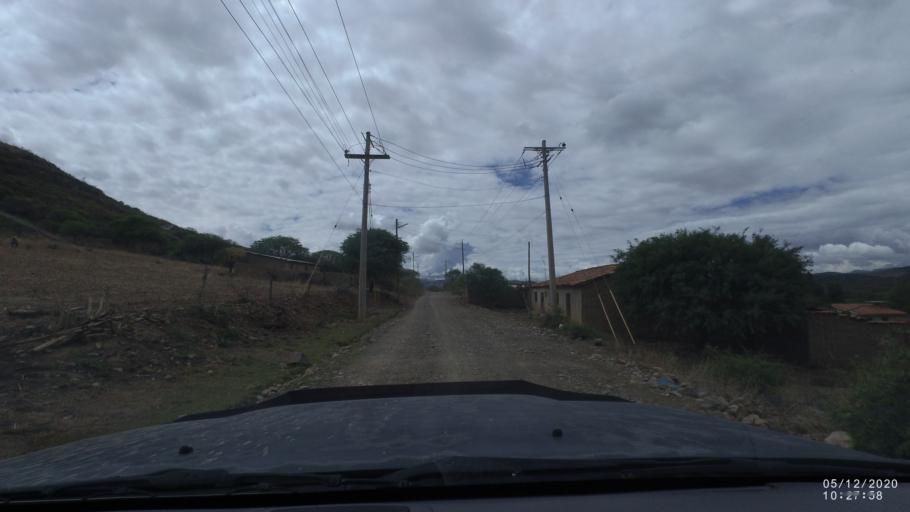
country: BO
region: Cochabamba
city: Sipe Sipe
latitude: -17.5354
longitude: -66.2763
